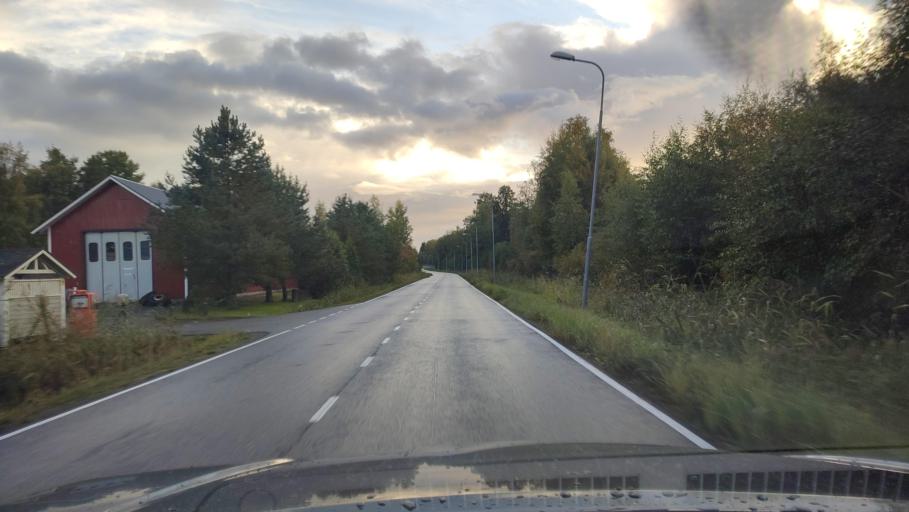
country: FI
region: Ostrobothnia
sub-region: Sydosterbotten
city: Kristinestad
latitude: 62.2773
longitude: 21.3959
